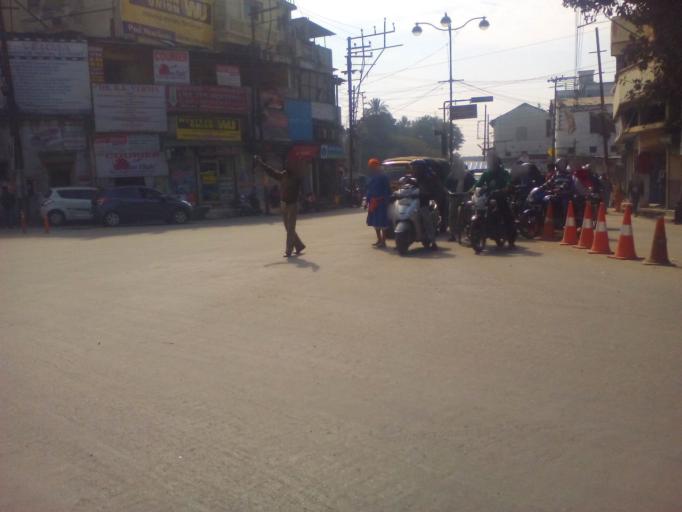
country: IN
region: Uttarakhand
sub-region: Dehradun
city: Dehradun
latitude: 30.3228
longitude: 78.0426
